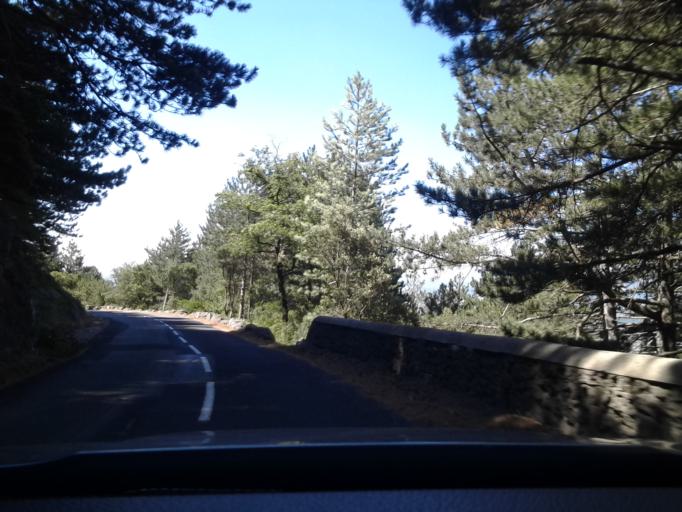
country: FR
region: Languedoc-Roussillon
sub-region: Departement de l'Herault
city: Montpeyroux
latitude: 43.7424
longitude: 3.4567
